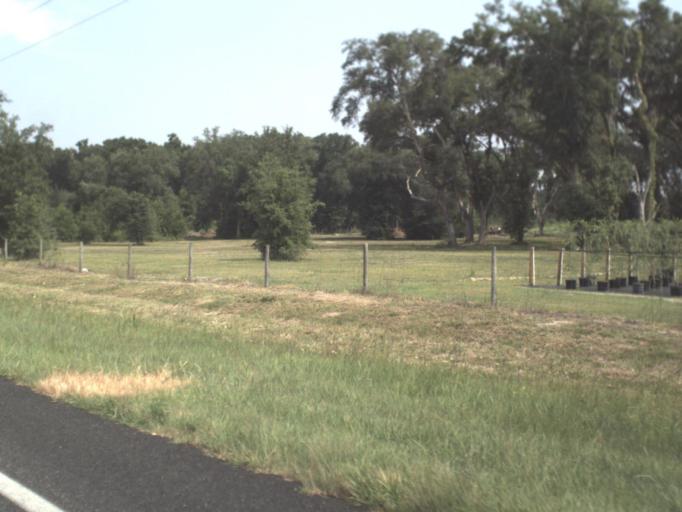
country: US
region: Florida
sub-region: Levy County
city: Williston
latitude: 29.4004
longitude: -82.5044
